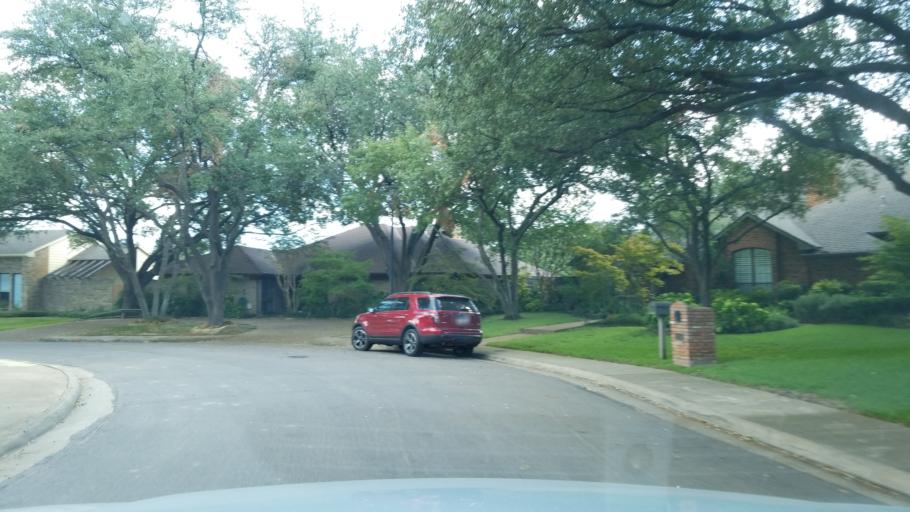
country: US
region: Texas
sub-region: Dallas County
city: Addison
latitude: 32.9658
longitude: -96.7988
